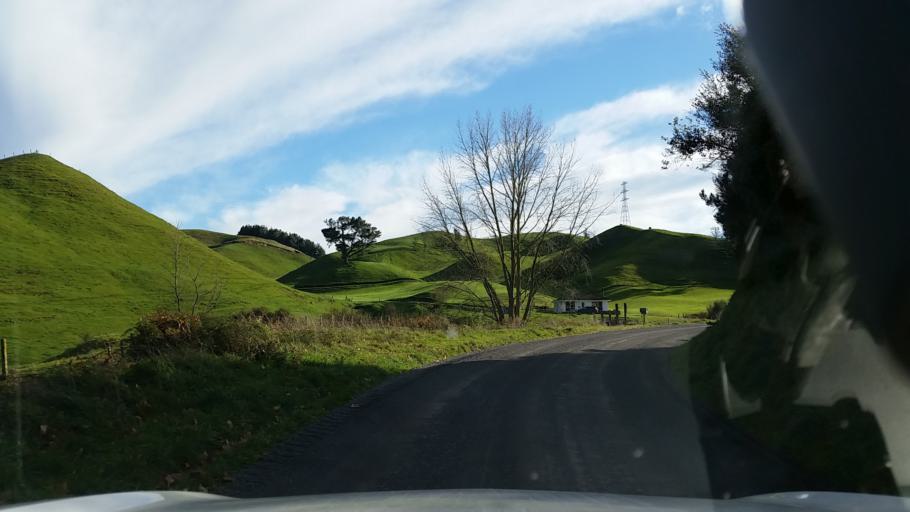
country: NZ
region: Waikato
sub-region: South Waikato District
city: Tokoroa
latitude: -38.3723
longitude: 176.0865
